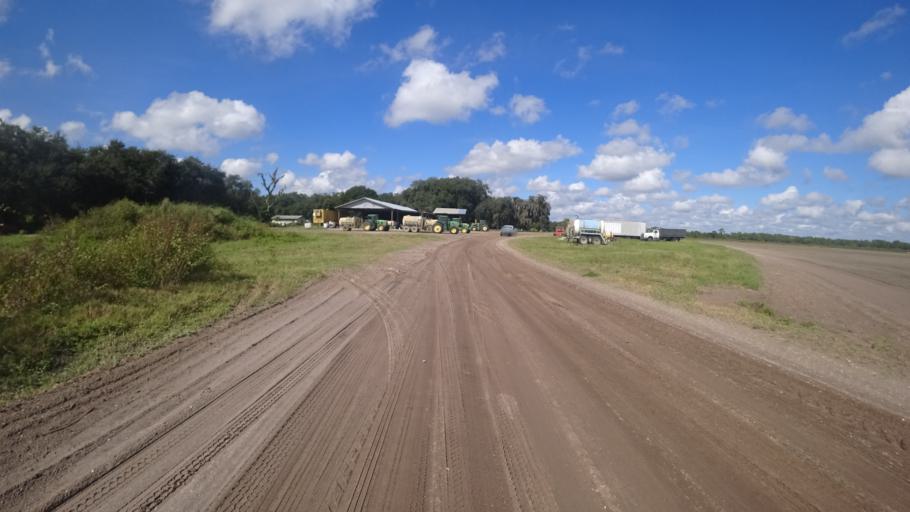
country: US
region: Florida
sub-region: DeSoto County
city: Arcadia
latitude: 27.3683
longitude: -82.1324
